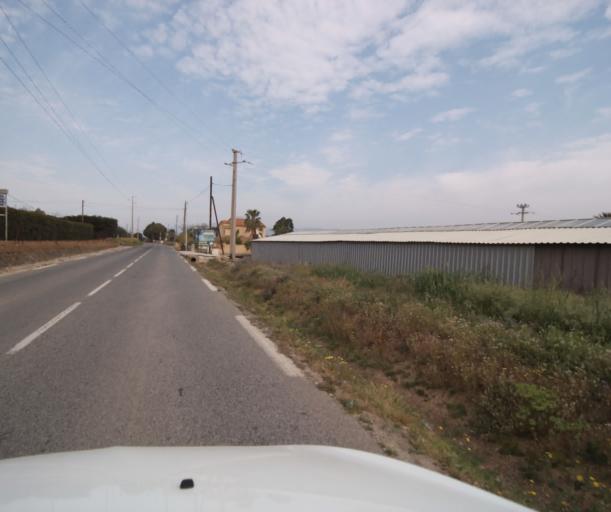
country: FR
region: Provence-Alpes-Cote d'Azur
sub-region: Departement du Var
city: Carqueiranne
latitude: 43.1153
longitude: 6.0946
